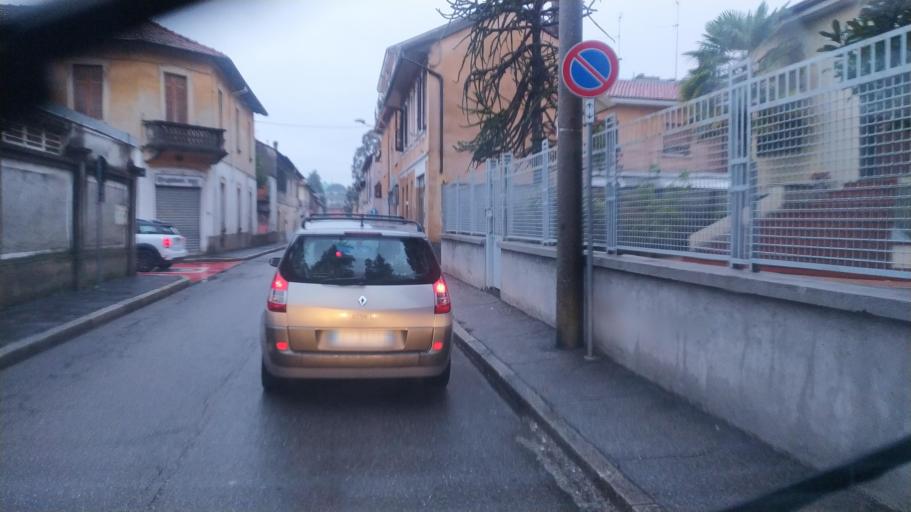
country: IT
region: Lombardy
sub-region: Citta metropolitana di Milano
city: Legnano
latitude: 45.6012
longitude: 8.9216
